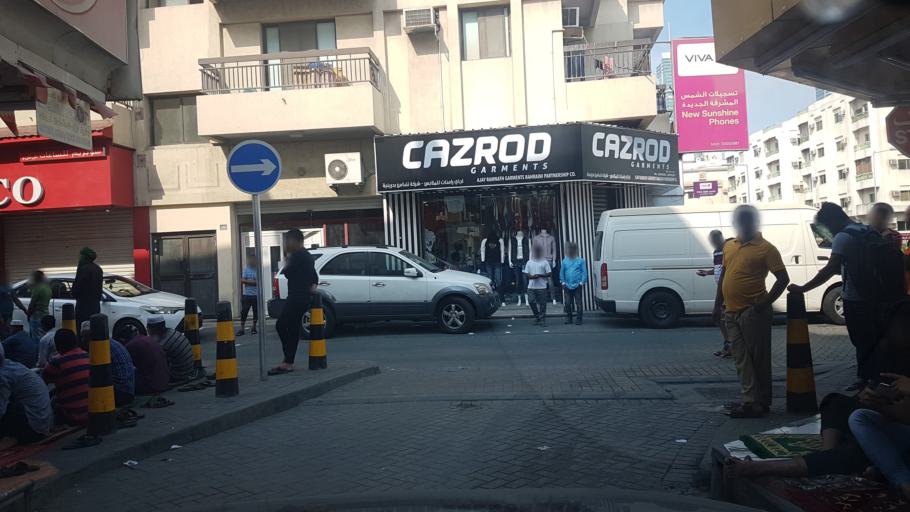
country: BH
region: Manama
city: Manama
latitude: 26.2303
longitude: 50.5742
